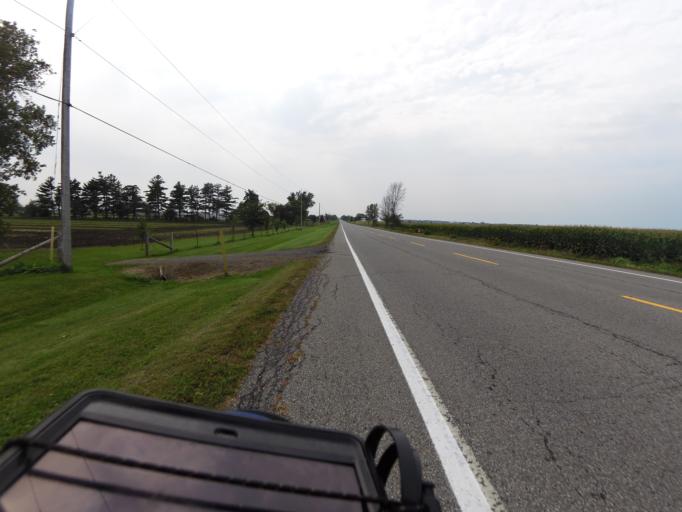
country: CA
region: Ontario
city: Casselman
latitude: 45.1675
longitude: -75.3113
